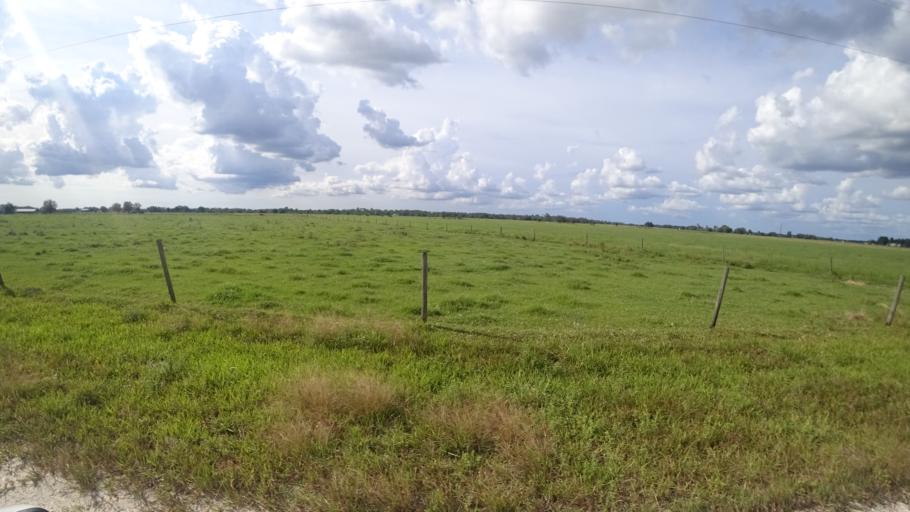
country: US
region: Florida
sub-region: Sarasota County
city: Lake Sarasota
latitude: 27.3336
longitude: -82.1799
